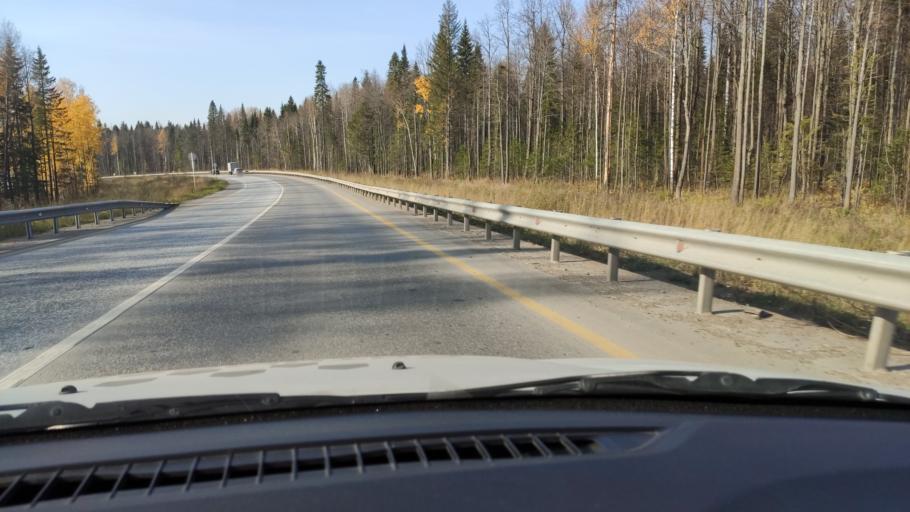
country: RU
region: Perm
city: Novyye Lyady
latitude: 58.0483
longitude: 56.5480
